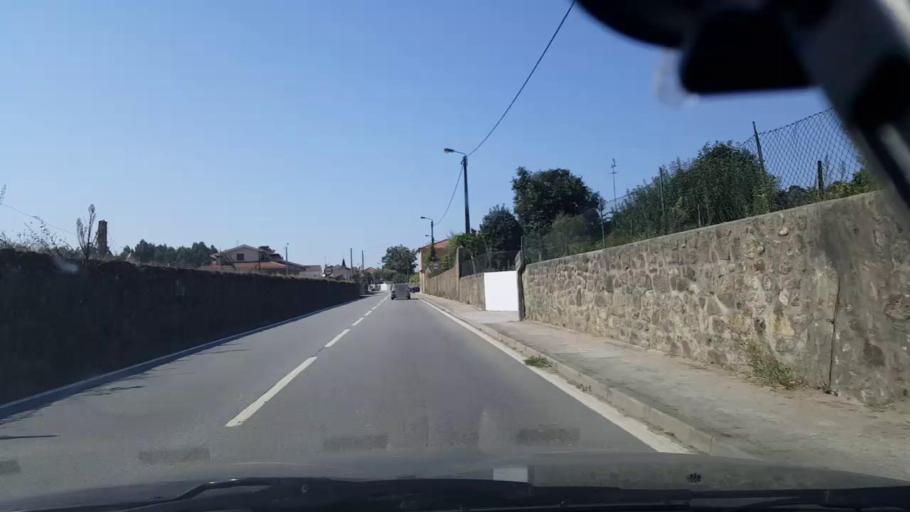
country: PT
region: Porto
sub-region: Povoa de Varzim
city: Pedroso
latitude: 41.4048
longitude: -8.6777
